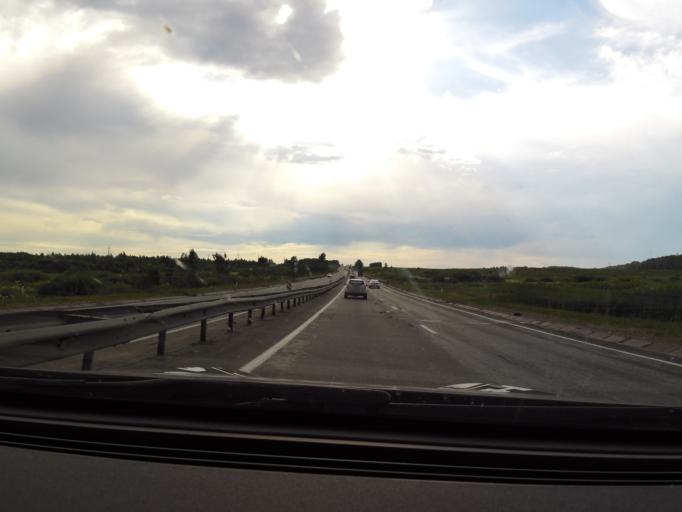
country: RU
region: Vladimir
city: Novovyazniki
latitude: 56.2166
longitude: 42.2411
